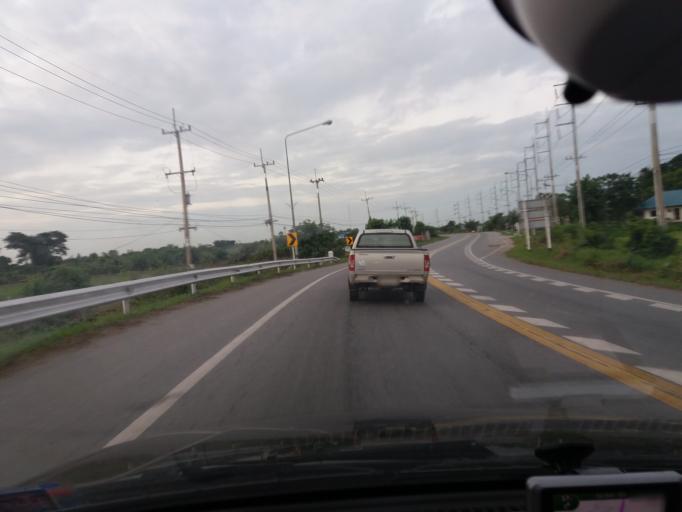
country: TH
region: Suphan Buri
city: U Thong
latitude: 14.5111
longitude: 99.9162
